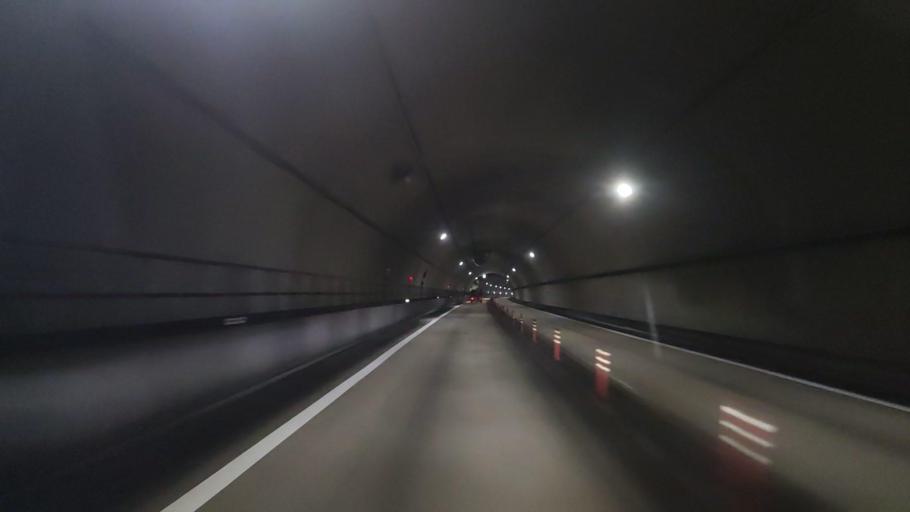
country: JP
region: Wakayama
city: Tanabe
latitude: 33.5485
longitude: 135.5176
